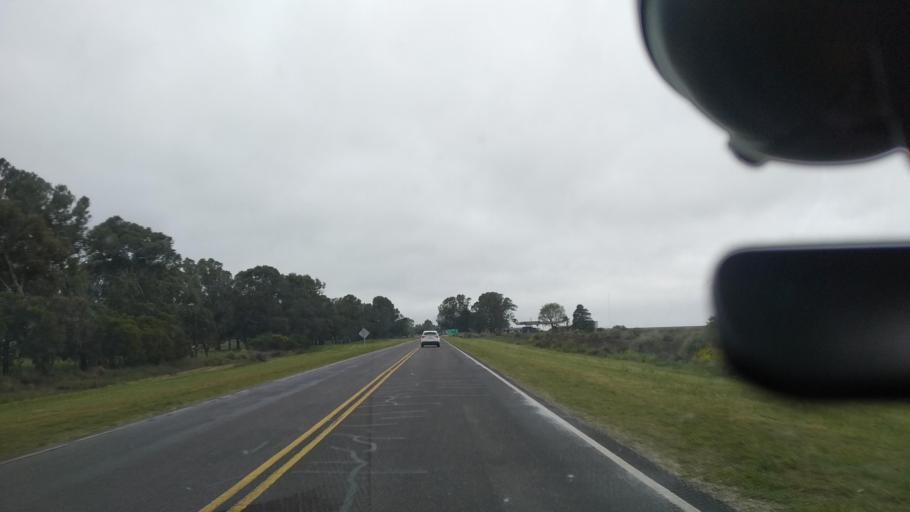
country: AR
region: Buenos Aires
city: Veronica
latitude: -35.7088
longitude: -57.3575
